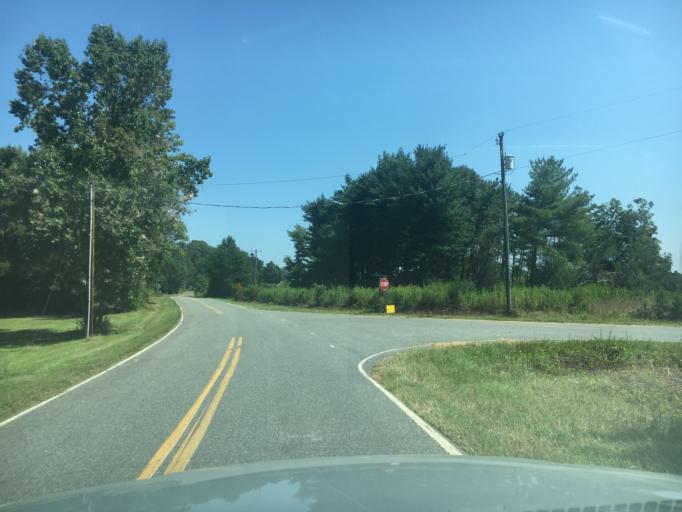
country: US
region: South Carolina
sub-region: Spartanburg County
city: Boiling Springs
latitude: 35.1969
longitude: -82.0318
